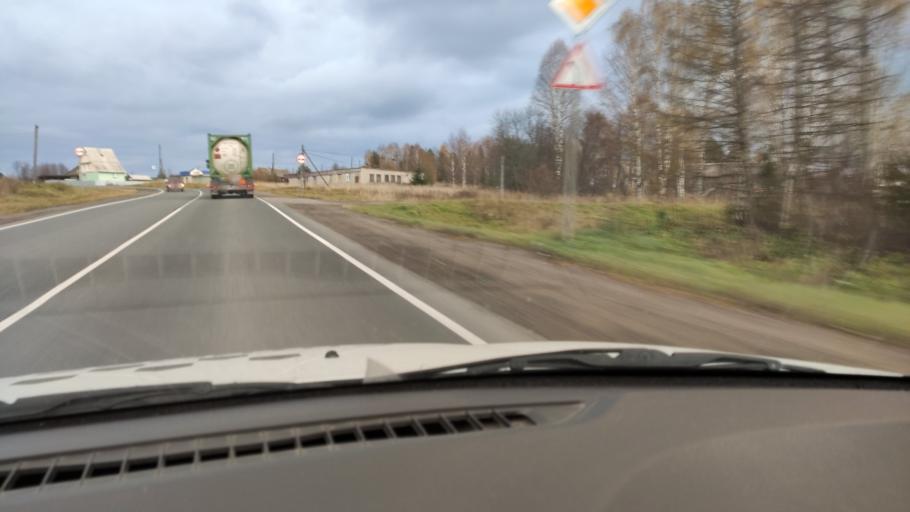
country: RU
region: Kirov
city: Belorechensk
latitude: 58.7132
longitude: 52.3260
